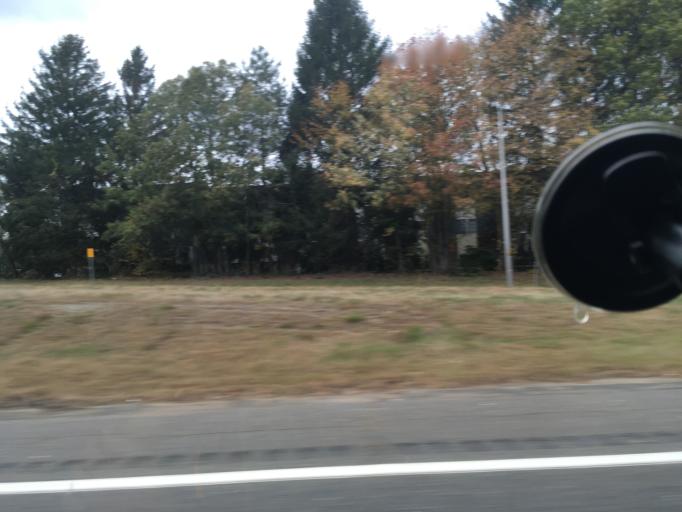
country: US
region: Massachusetts
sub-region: Bristol County
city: Seekonk
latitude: 41.7971
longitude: -71.3514
